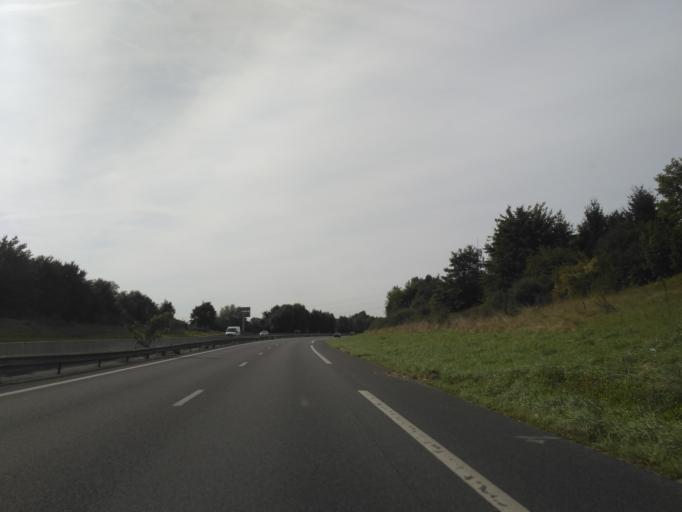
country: FR
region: Ile-de-France
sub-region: Departement de Seine-et-Marne
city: Lesigny
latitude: 48.7404
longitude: 2.6125
